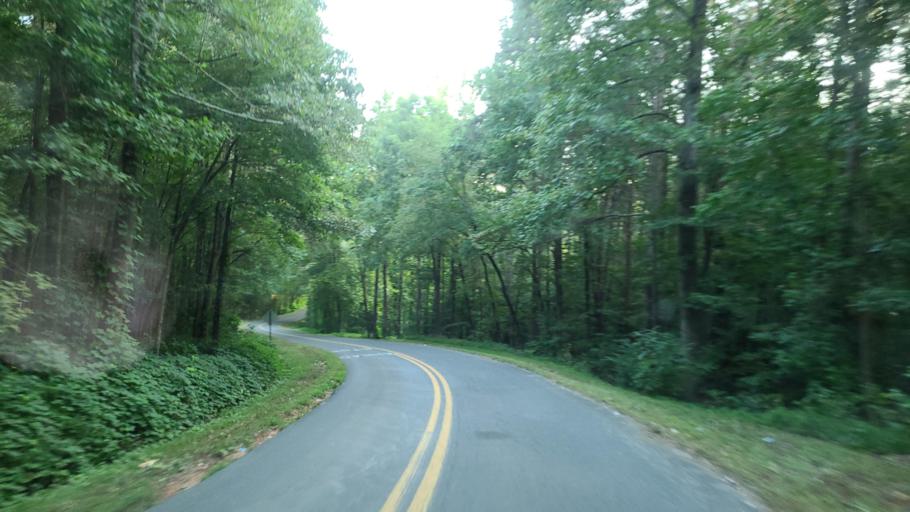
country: US
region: Georgia
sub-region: Pickens County
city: Jasper
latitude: 34.4785
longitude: -84.5421
